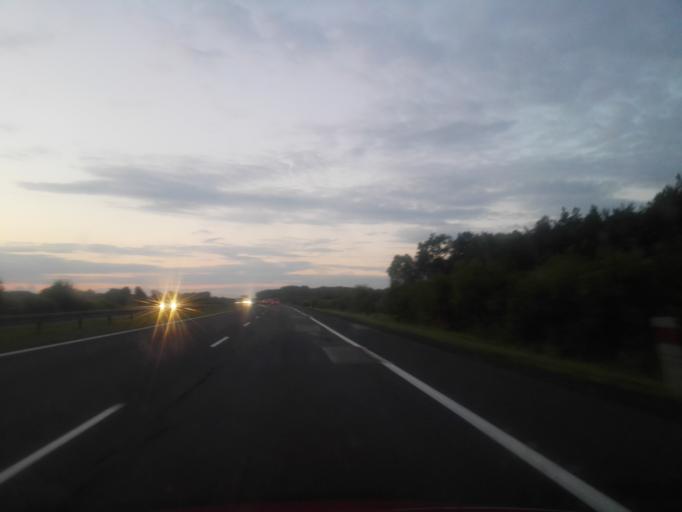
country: PL
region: Lodz Voivodeship
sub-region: Powiat radomszczanski
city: Kamiensk
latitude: 51.2481
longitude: 19.5252
